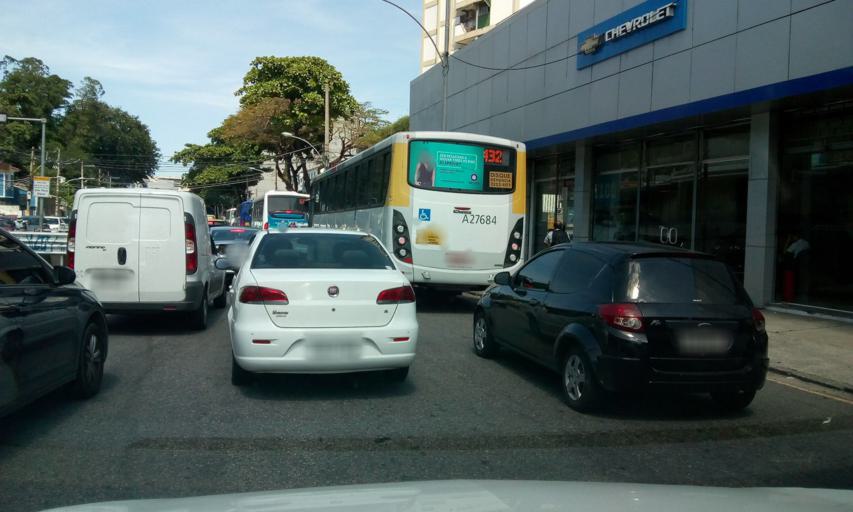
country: BR
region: Rio de Janeiro
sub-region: Rio De Janeiro
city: Rio de Janeiro
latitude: -22.9167
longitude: -43.2402
